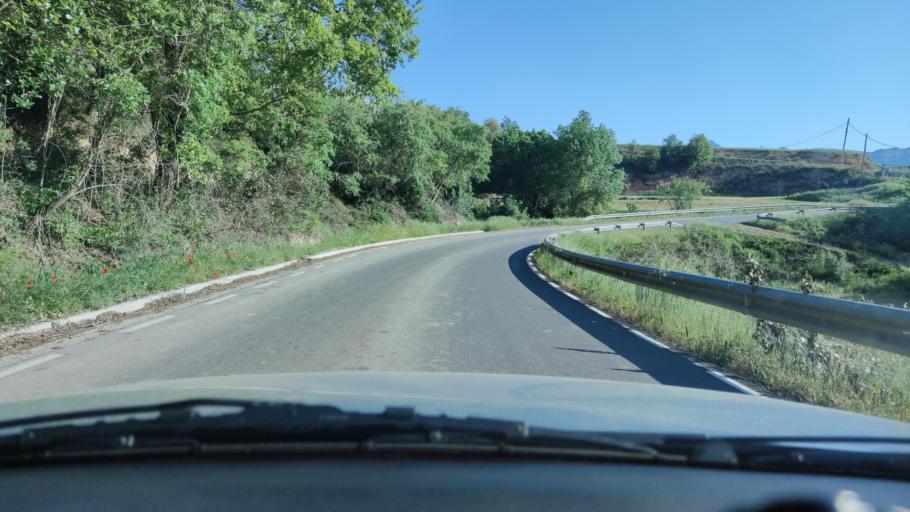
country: ES
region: Catalonia
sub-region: Provincia de Lleida
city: Oliana
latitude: 42.0491
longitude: 1.2926
